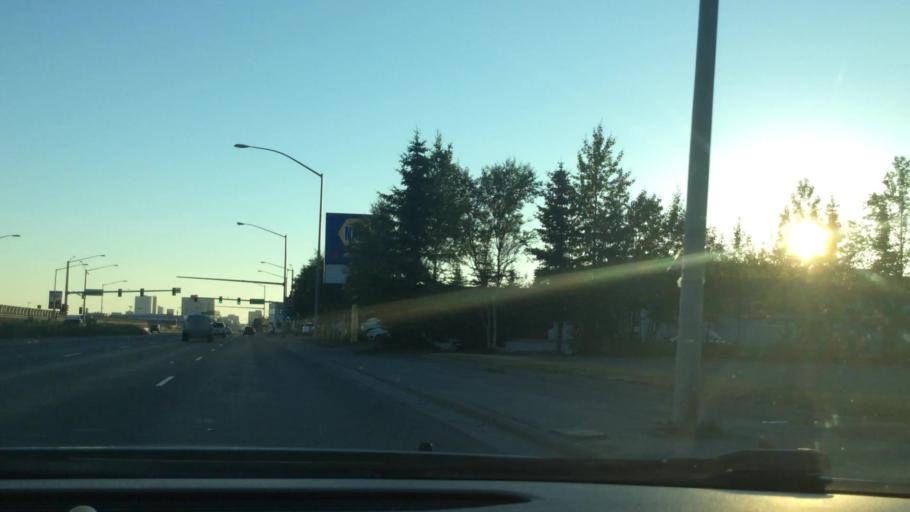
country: US
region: Alaska
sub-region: Anchorage Municipality
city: Anchorage
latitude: 61.2176
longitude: -149.8466
